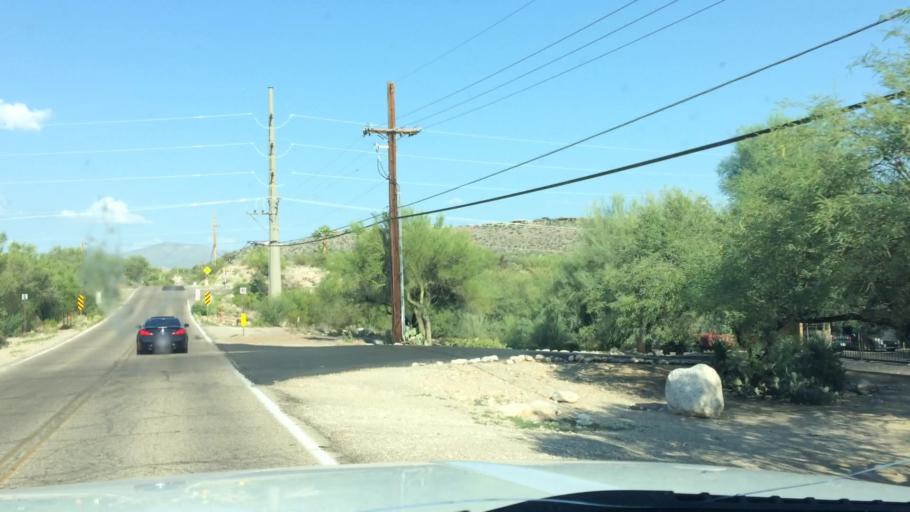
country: US
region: Arizona
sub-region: Pima County
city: Catalina Foothills
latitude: 32.2943
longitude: -110.8379
